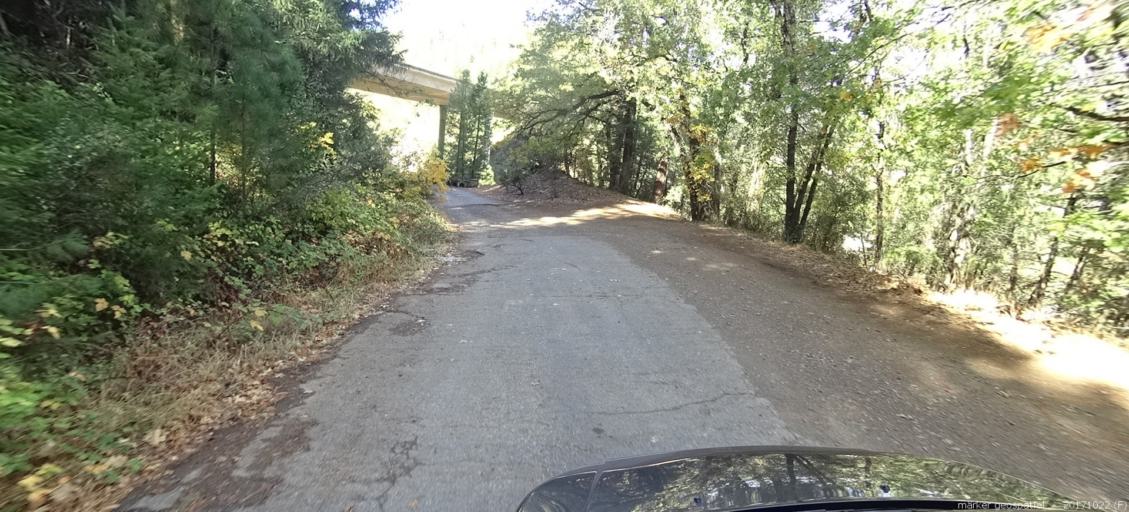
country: US
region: California
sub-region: Siskiyou County
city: Dunsmuir
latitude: 40.9745
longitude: -122.4311
